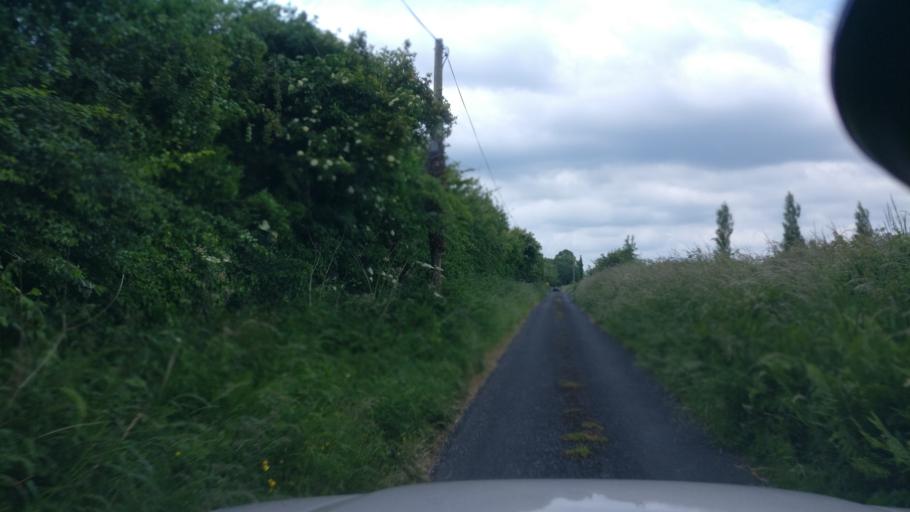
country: IE
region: Connaught
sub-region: County Galway
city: Ballinasloe
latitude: 53.2739
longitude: -8.3735
